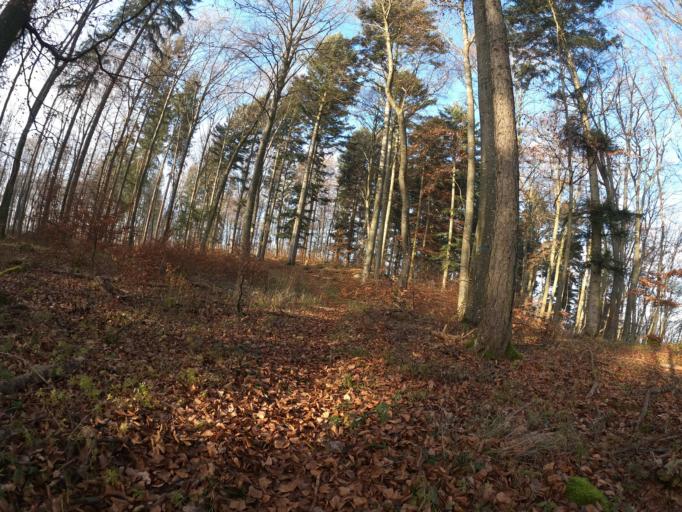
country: DE
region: Baden-Wuerttemberg
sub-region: Regierungsbezirk Stuttgart
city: Deggingen
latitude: 48.5989
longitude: 9.7433
